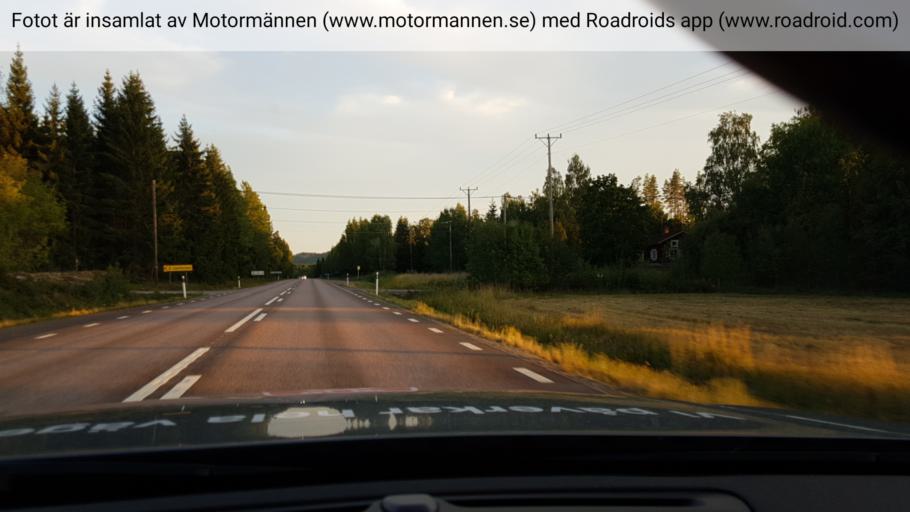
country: SE
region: OErebro
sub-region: Karlskoga Kommun
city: Karlskoga
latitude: 59.4217
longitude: 14.4278
